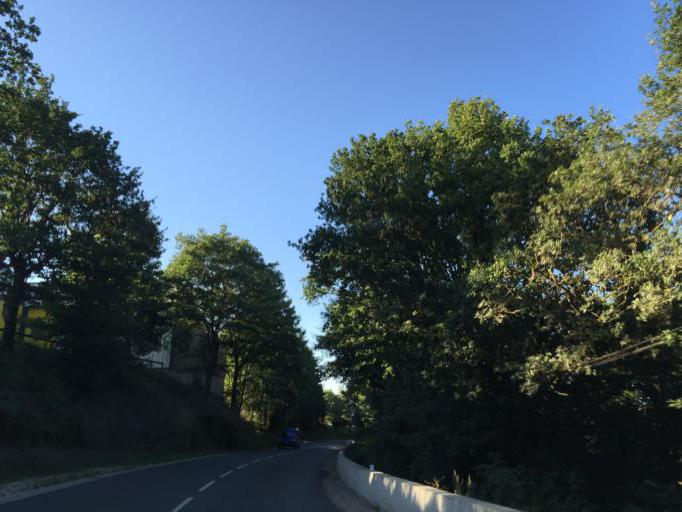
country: FR
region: Midi-Pyrenees
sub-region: Departement de l'Aveyron
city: Salles-Curan
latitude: 44.1772
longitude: 2.7918
